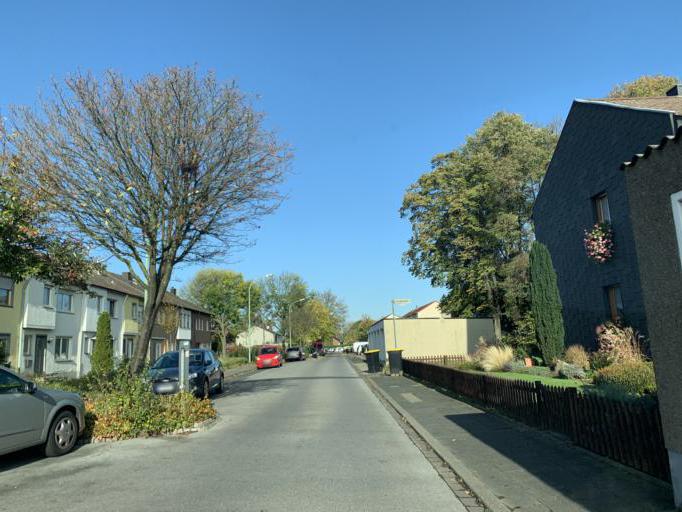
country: DE
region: North Rhine-Westphalia
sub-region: Regierungsbezirk Koln
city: Dueren
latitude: 50.8255
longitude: 6.4709
